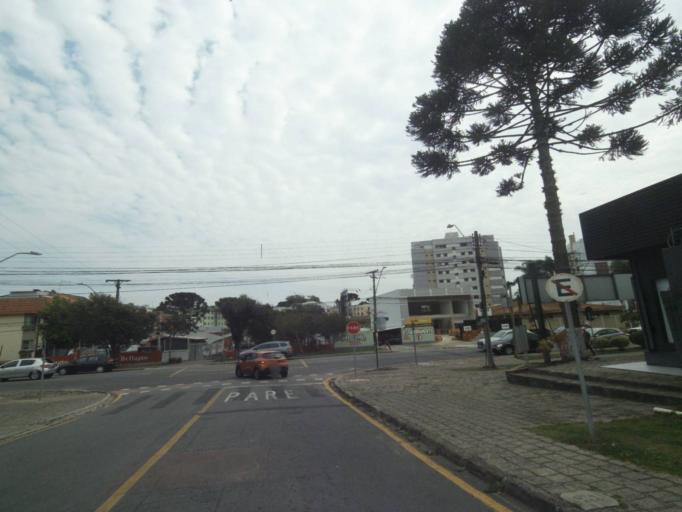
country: BR
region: Parana
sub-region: Curitiba
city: Curitiba
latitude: -25.4516
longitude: -49.3023
